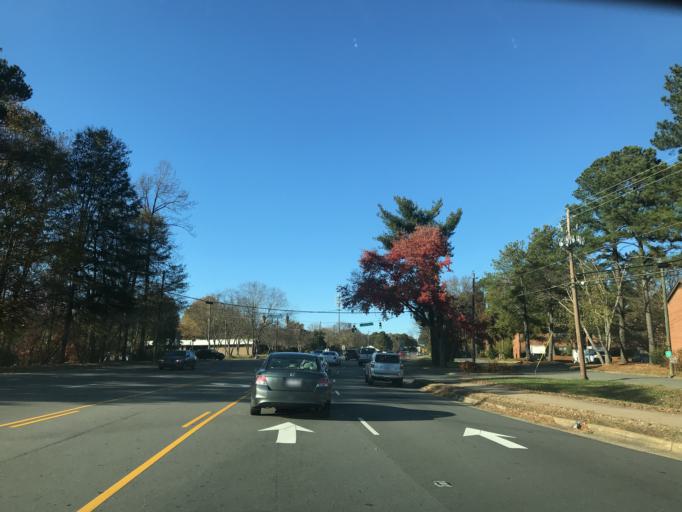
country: US
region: North Carolina
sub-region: Wake County
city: West Raleigh
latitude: 35.8607
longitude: -78.6188
